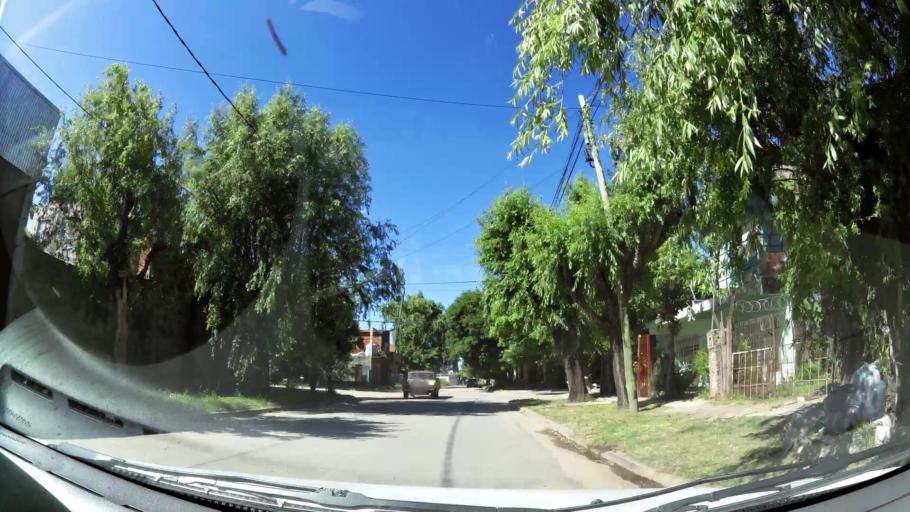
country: AR
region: Buenos Aires
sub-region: Partido de General San Martin
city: General San Martin
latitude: -34.5166
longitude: -58.5832
